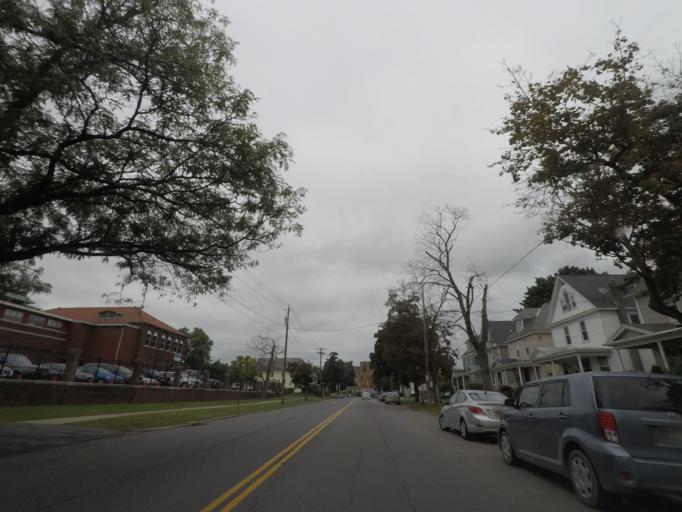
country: US
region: New York
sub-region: Albany County
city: West Albany
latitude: 42.6710
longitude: -73.7821
